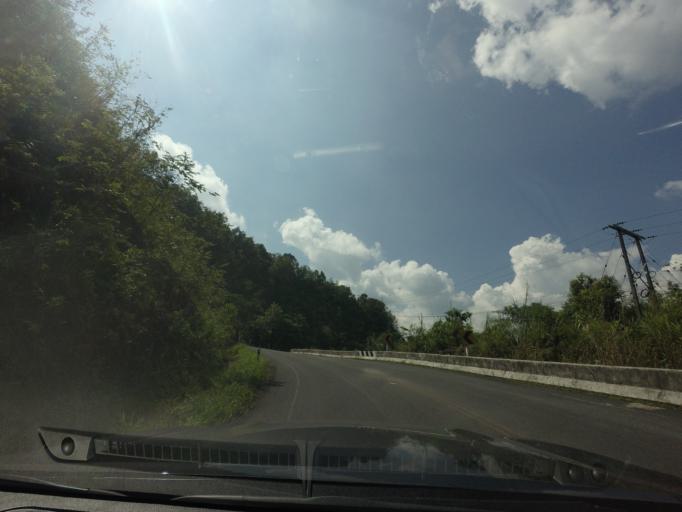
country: TH
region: Nan
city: Bo Kluea
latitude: 19.0691
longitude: 101.1240
